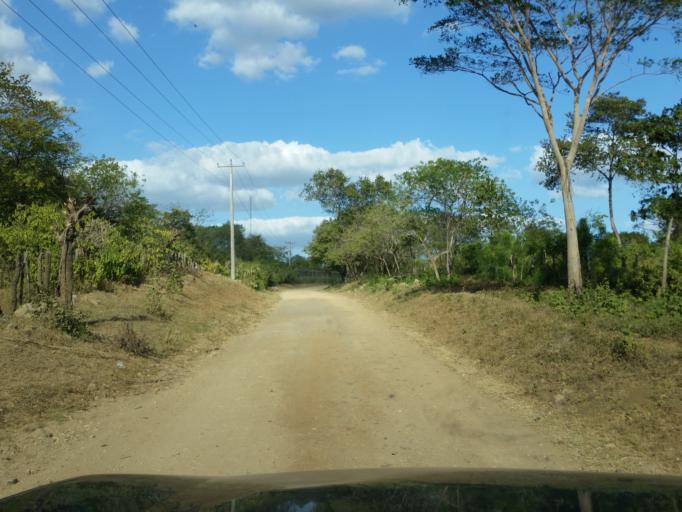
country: NI
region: Managua
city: Carlos Fonseca Amador
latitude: 11.9216
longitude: -86.5934
